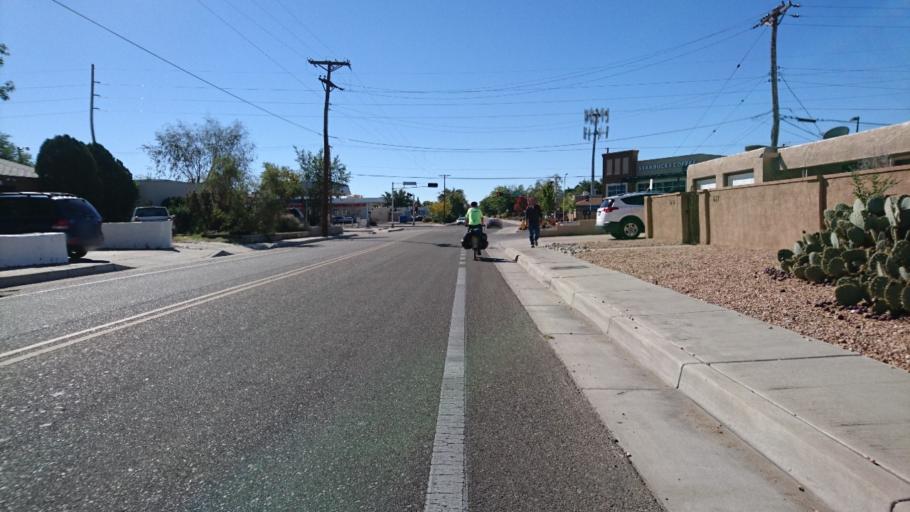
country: US
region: New Mexico
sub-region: Bernalillo County
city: Albuquerque
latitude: 35.0883
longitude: -106.5953
